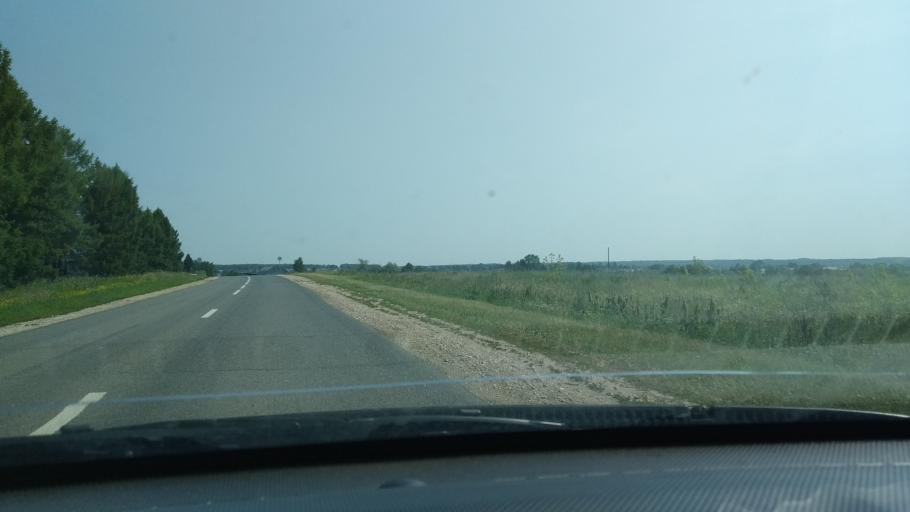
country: RU
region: Tatarstan
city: Osinovo
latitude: 55.9761
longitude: 48.7840
